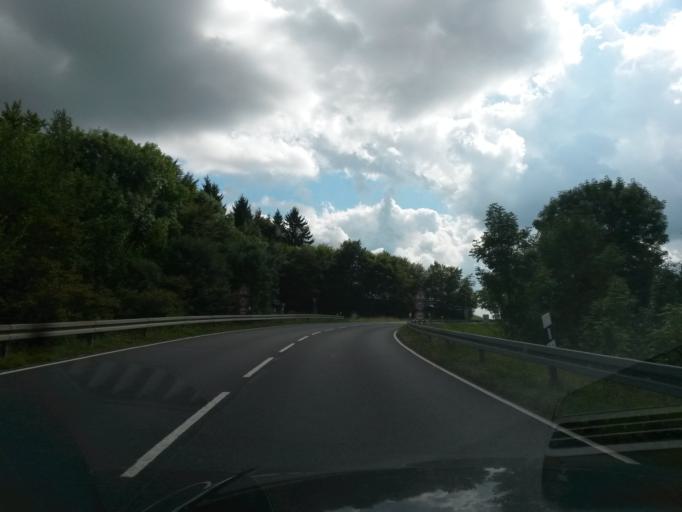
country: DE
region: Hesse
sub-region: Regierungsbezirk Kassel
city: Poppenhausen
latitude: 50.5218
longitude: 9.9059
